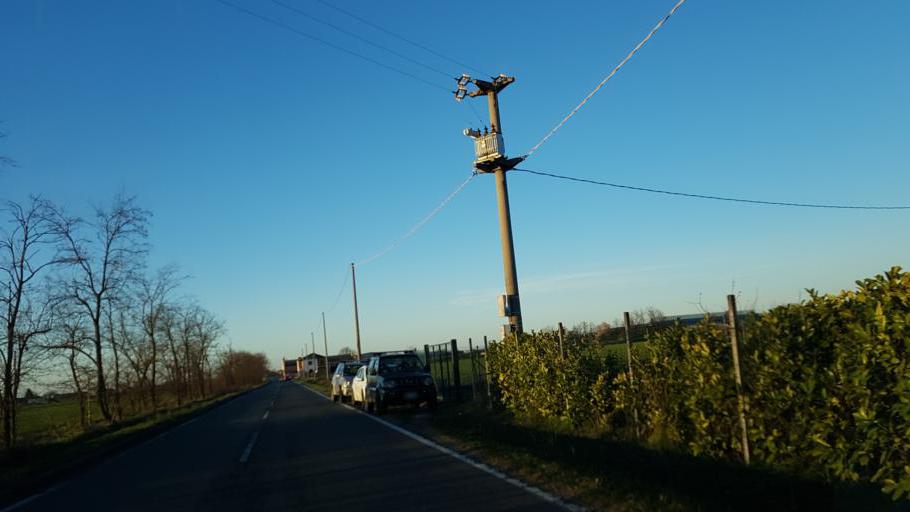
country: IT
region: Piedmont
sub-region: Provincia di Alessandria
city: Villalvernia
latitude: 44.8000
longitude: 8.8289
